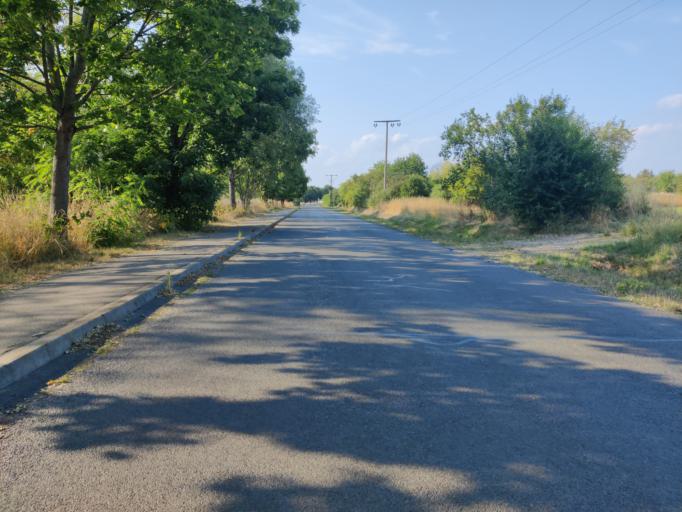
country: DE
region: Saxony
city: Neukieritzsch
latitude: 51.1626
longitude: 12.4337
